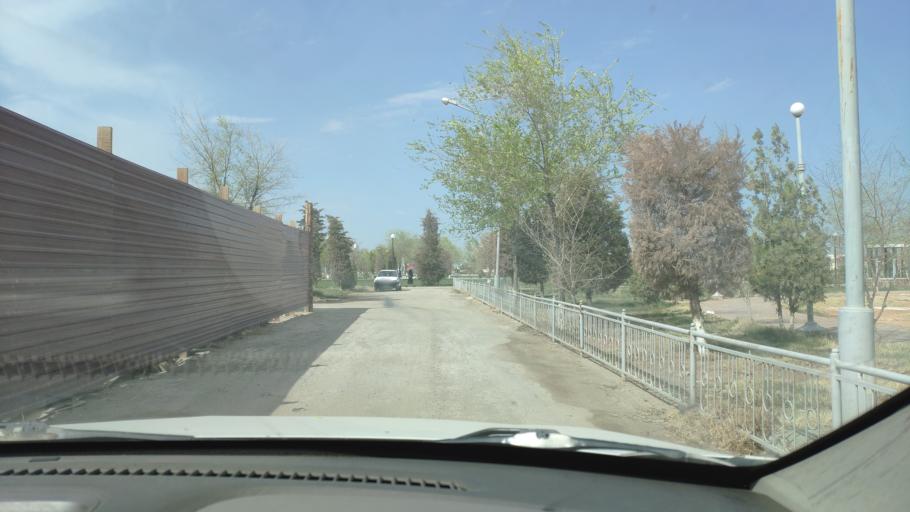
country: UZ
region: Xorazm
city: Urganch
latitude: 41.5448
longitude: 60.6278
